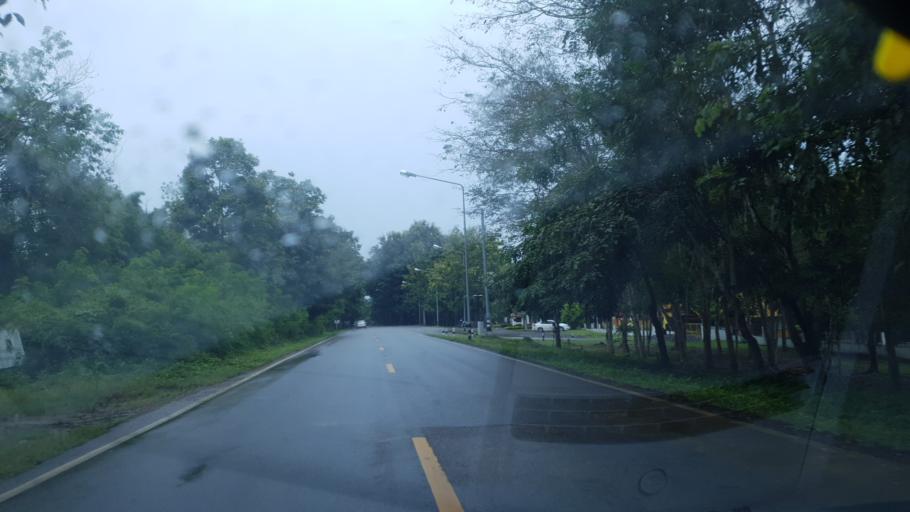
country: TH
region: Mae Hong Son
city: Pa Pae
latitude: 18.2108
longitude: 97.9382
